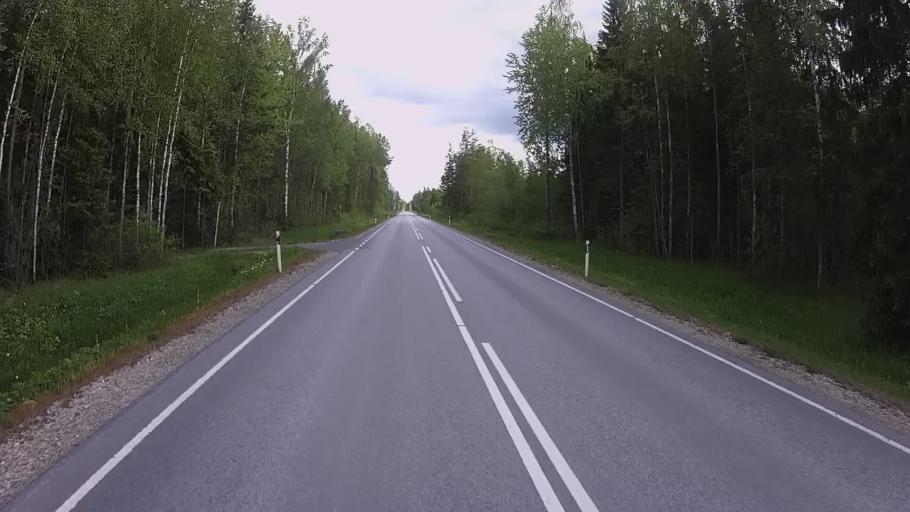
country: EE
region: Jogevamaa
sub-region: Mustvee linn
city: Mustvee
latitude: 58.9734
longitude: 26.8274
